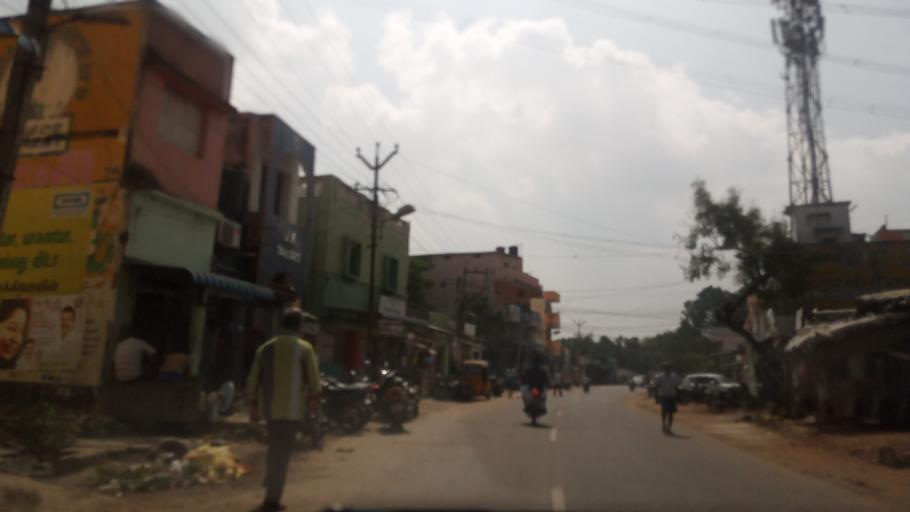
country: IN
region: Tamil Nadu
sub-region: Vellore
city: Arakkonam
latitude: 13.0791
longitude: 79.6716
